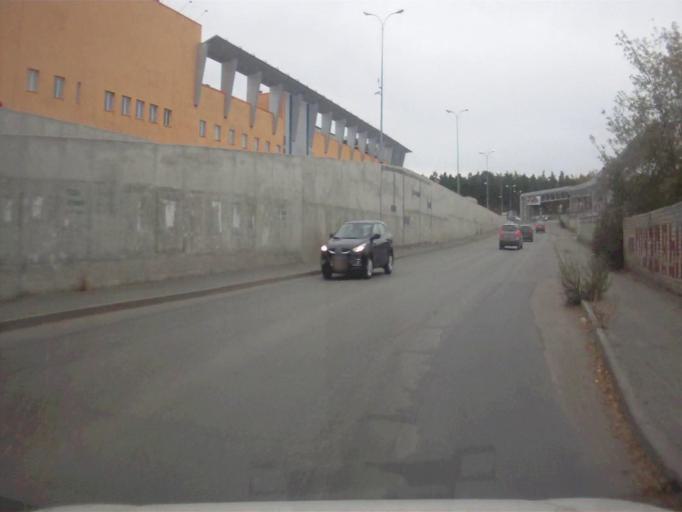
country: RU
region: Chelyabinsk
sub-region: Gorod Chelyabinsk
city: Chelyabinsk
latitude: 55.1707
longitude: 61.3538
